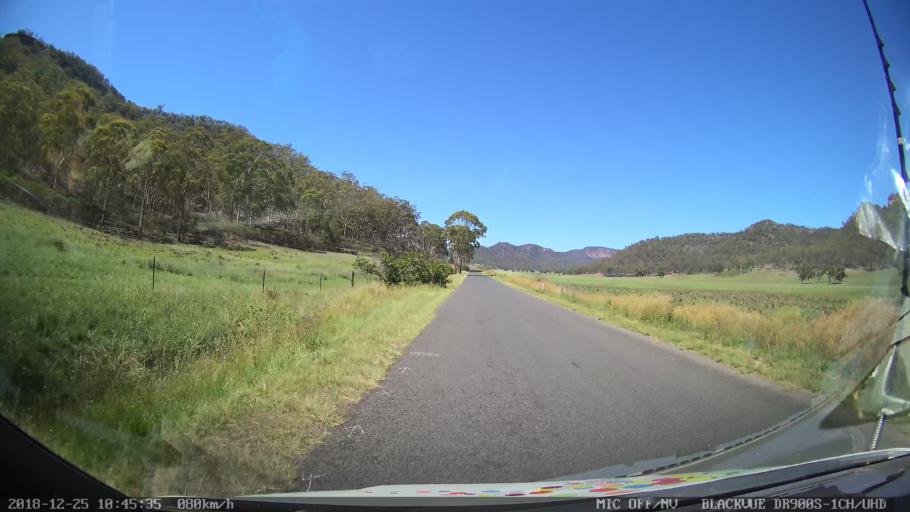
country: AU
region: New South Wales
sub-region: Upper Hunter Shire
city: Merriwa
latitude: -32.4348
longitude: 150.2892
